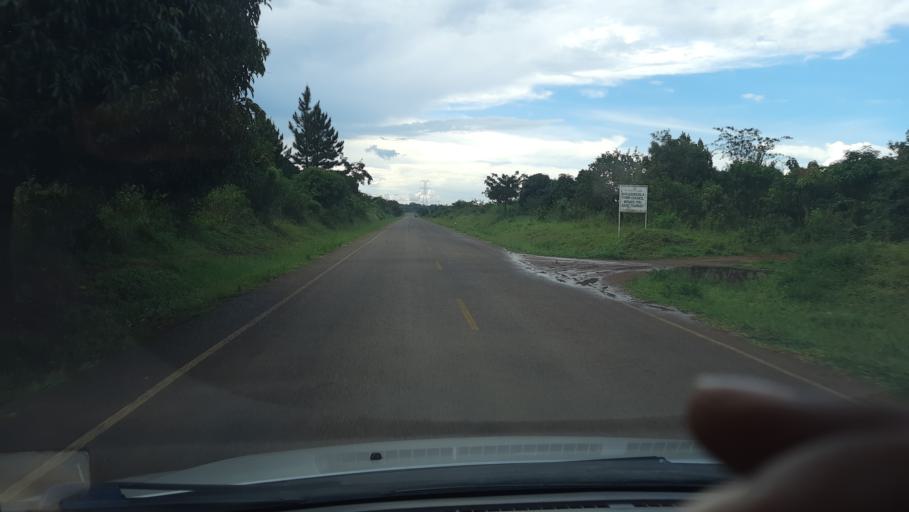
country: UG
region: Central Region
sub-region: Nakasongola District
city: Nakasongola
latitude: 1.3194
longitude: 32.4344
